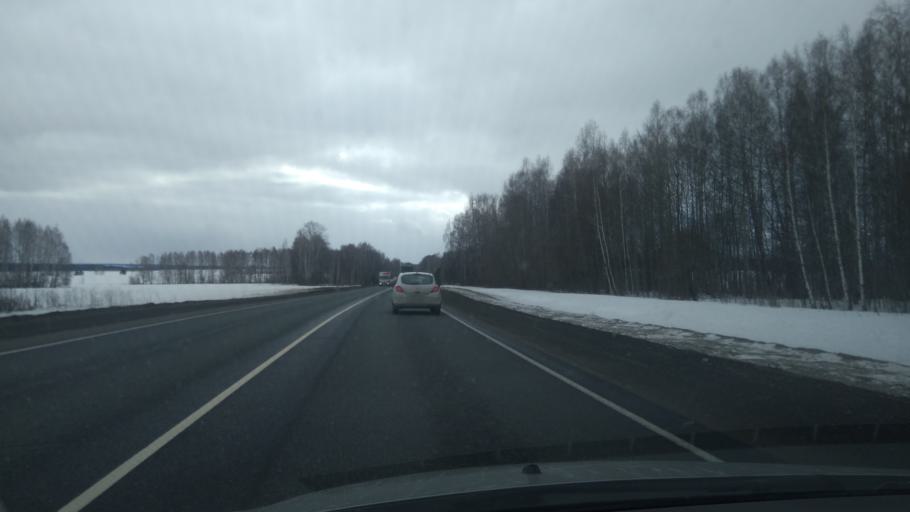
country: RU
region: Perm
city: Suksun
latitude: 56.9762
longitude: 57.5155
